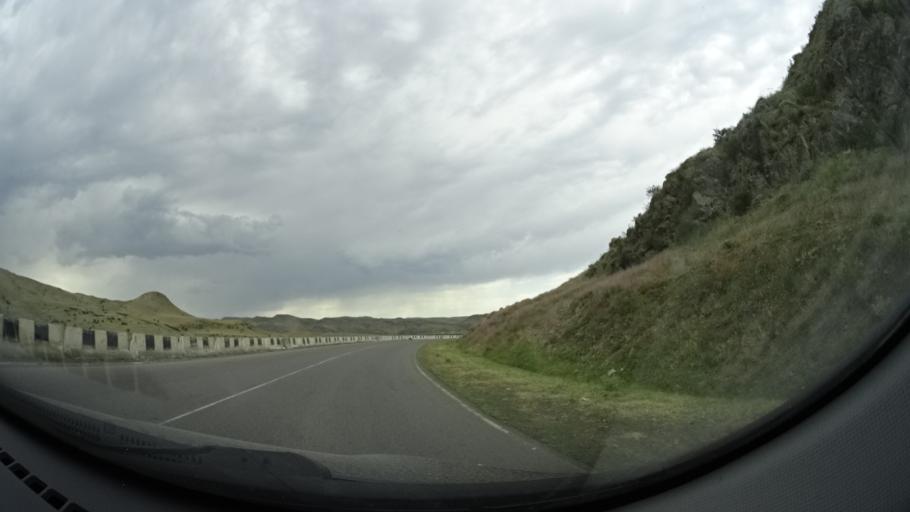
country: GE
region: Samtskhe-Javakheti
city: Aspindza
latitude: 41.6050
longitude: 43.1365
